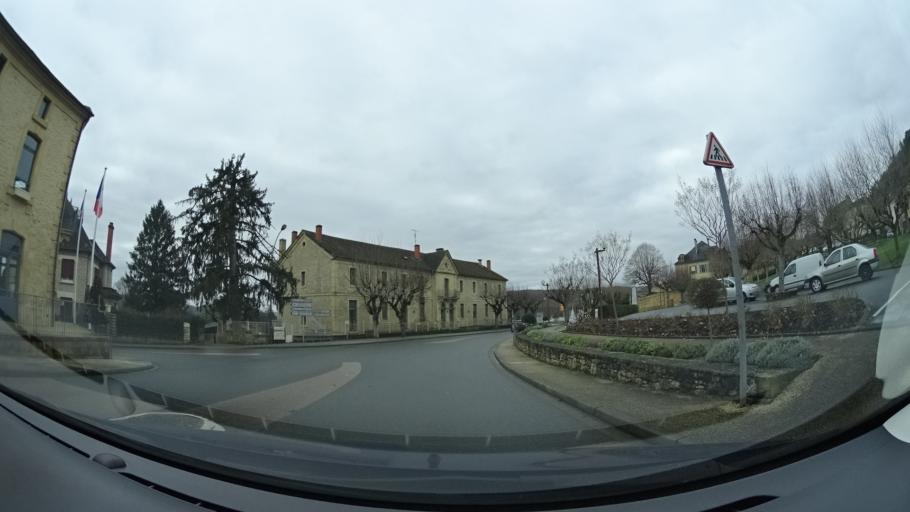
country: FR
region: Aquitaine
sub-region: Departement de la Dordogne
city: Saint-Cyprien
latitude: 44.8692
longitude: 1.0478
